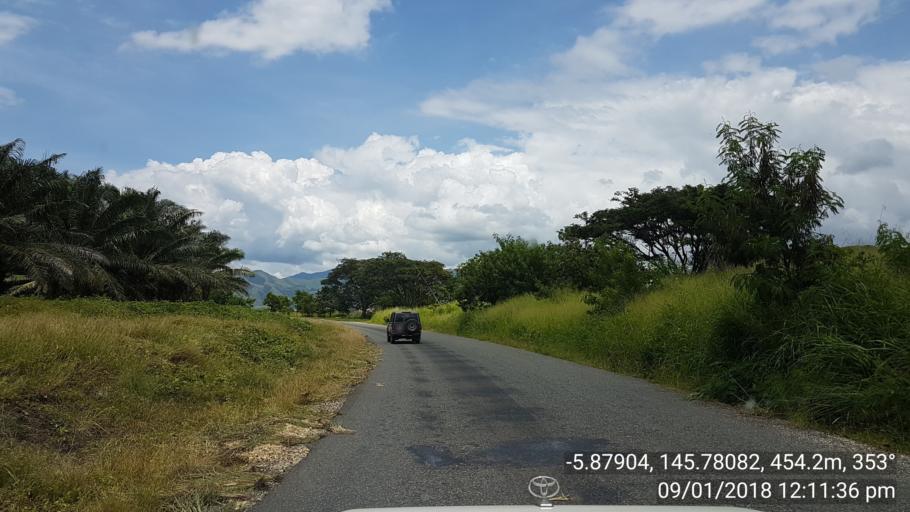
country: PG
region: Eastern Highlands
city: Kainantu
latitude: -5.8798
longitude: 145.7809
